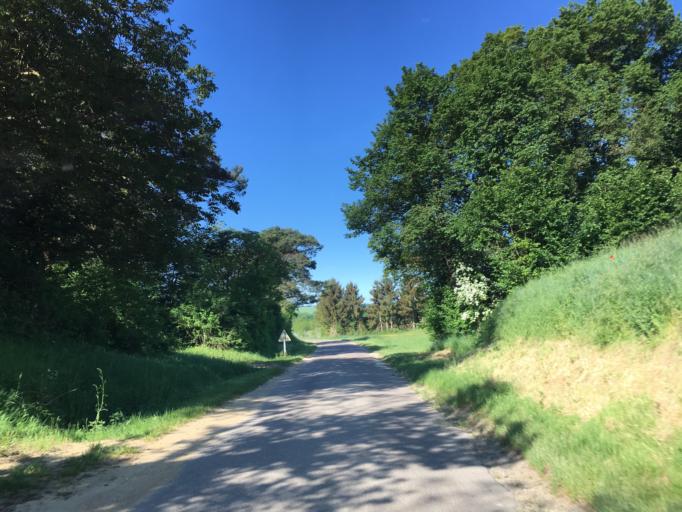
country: FR
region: Bourgogne
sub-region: Departement de l'Yonne
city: Aillant-sur-Tholon
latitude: 47.8231
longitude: 3.3794
